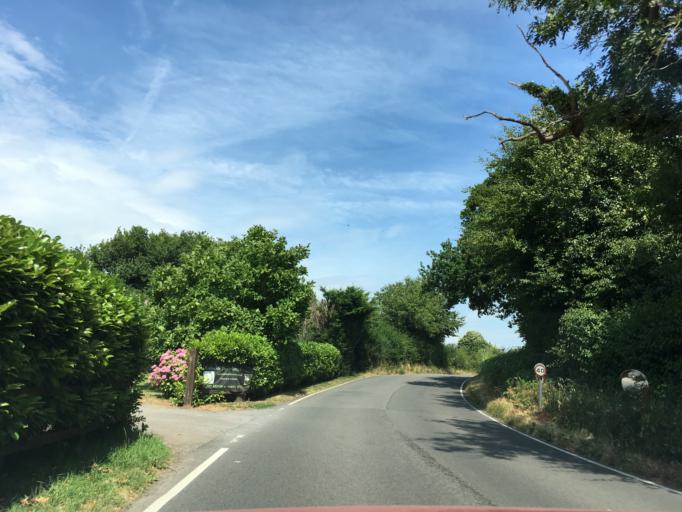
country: GB
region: Wales
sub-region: Newport
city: Caerleon
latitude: 51.6053
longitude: -2.9379
